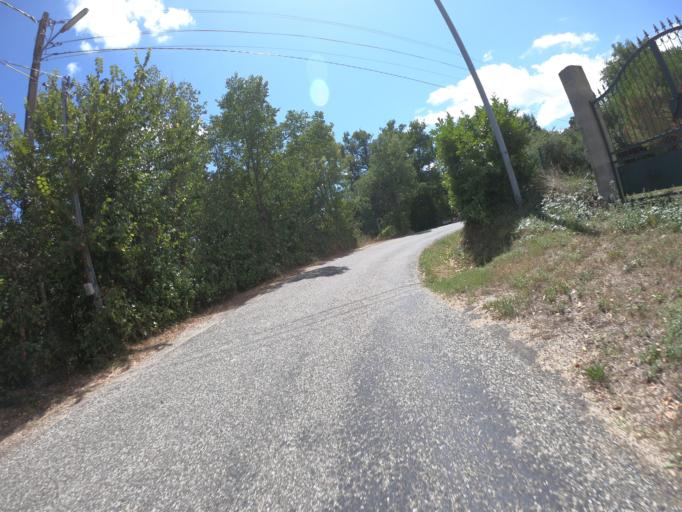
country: FR
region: Midi-Pyrenees
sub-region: Departement de l'Ariege
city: Mirepoix
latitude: 43.0628
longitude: 1.8455
